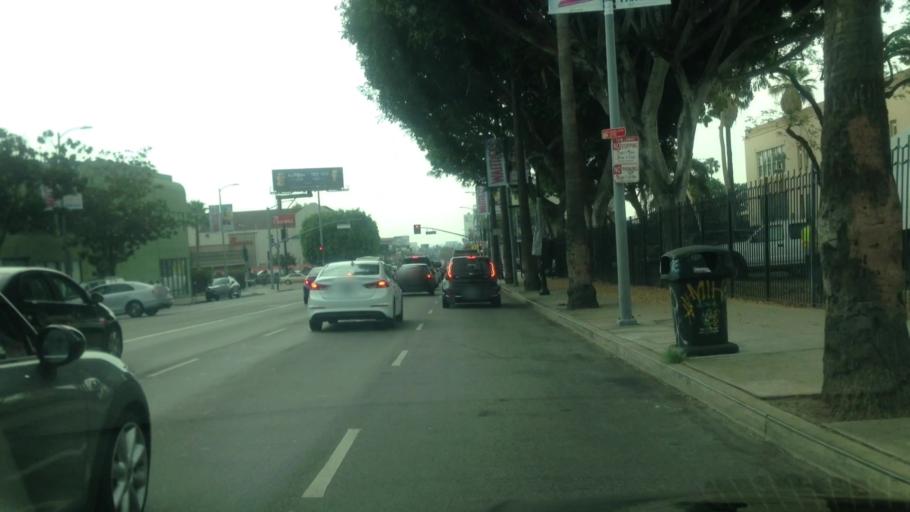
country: US
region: California
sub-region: Los Angeles County
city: Hollywood
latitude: 34.0992
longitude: -118.3388
